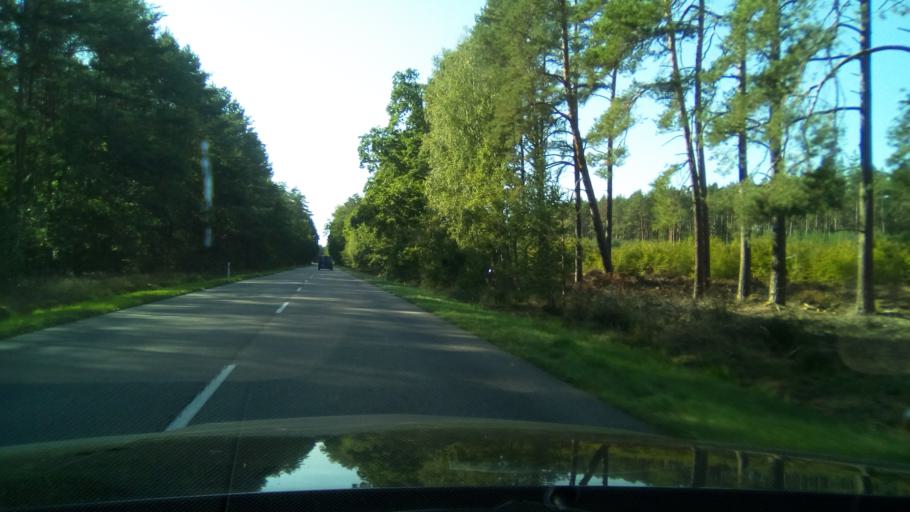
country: PL
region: West Pomeranian Voivodeship
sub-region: Powiat kamienski
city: Golczewo
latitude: 53.8142
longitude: 15.0730
